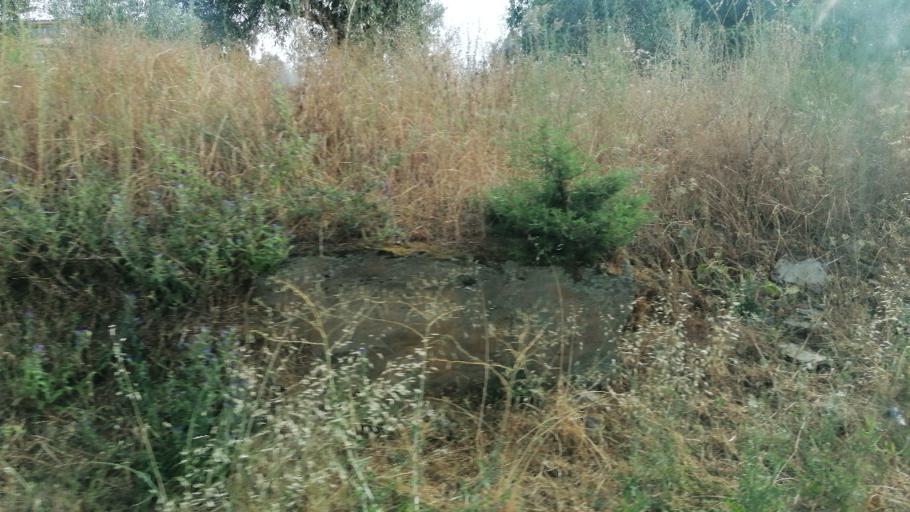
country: PT
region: Viseu
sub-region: Sao Joao da Pesqueira
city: Sao Joao da Pesqueira
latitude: 41.1415
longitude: -7.3983
